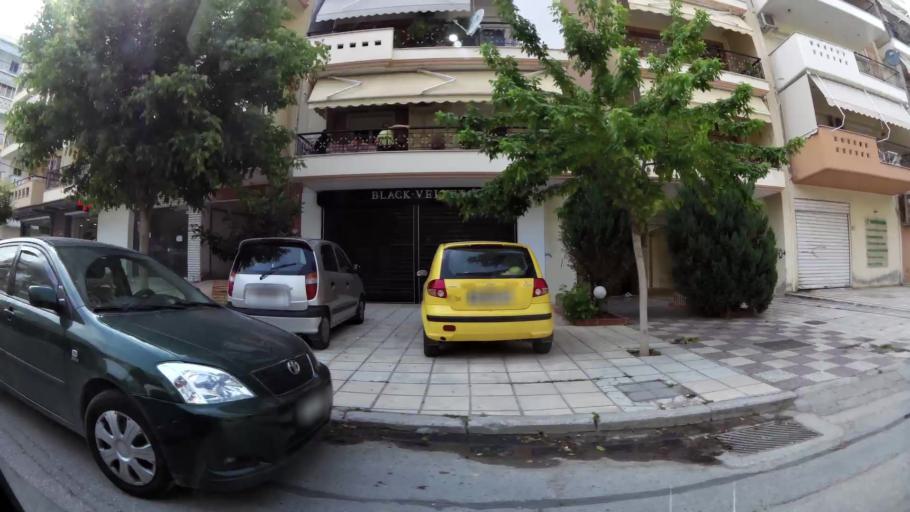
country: GR
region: Central Macedonia
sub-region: Nomos Thessalonikis
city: Stavroupoli
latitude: 40.6836
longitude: 22.9327
